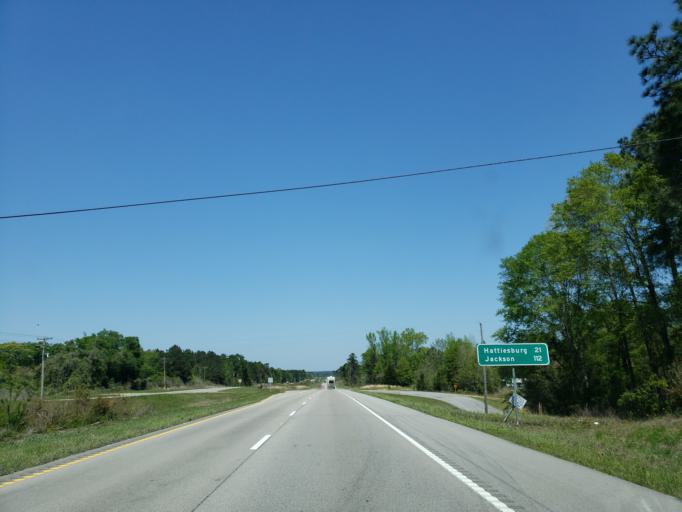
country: US
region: Mississippi
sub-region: Stone County
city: Wiggins
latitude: 30.9546
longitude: -89.1892
